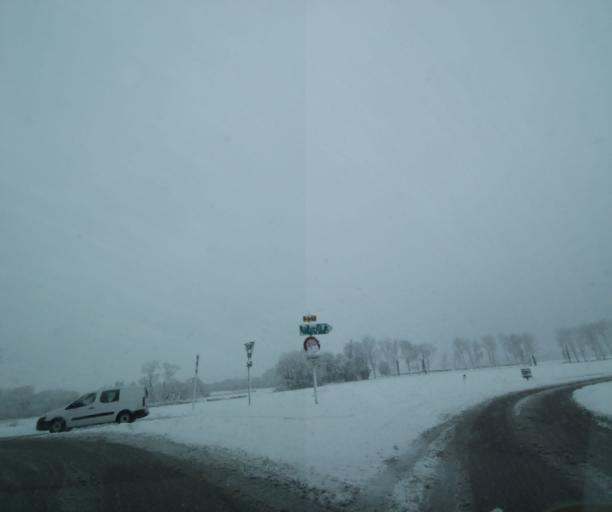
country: FR
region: Champagne-Ardenne
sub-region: Departement de la Haute-Marne
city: Saint-Dizier
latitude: 48.6203
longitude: 4.9277
